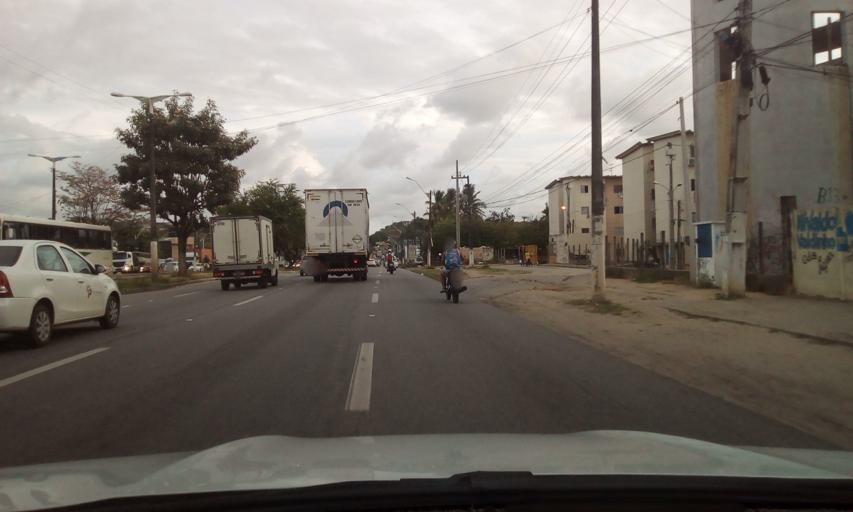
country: BR
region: Pernambuco
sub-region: Abreu E Lima
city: Abreu e Lima
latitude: -7.8941
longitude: -34.9033
